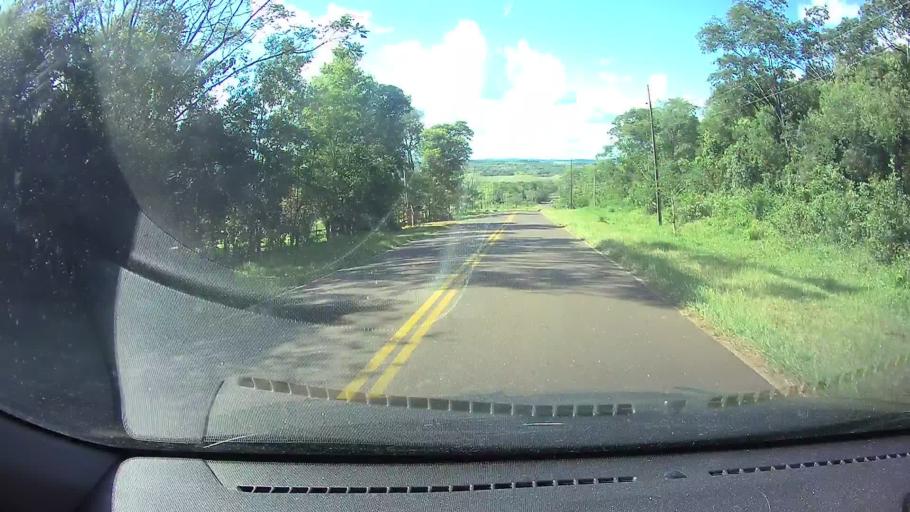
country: PY
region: Paraguari
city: Sapucai
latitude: -25.6449
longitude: -56.8645
